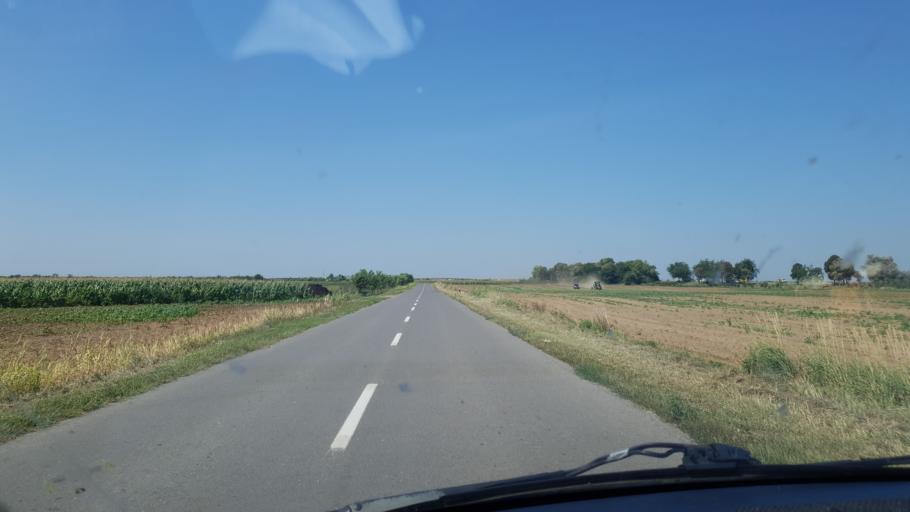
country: RS
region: Autonomna Pokrajina Vojvodina
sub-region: Juznobacki Okrug
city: Kovilj
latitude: 45.2132
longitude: 20.0635
